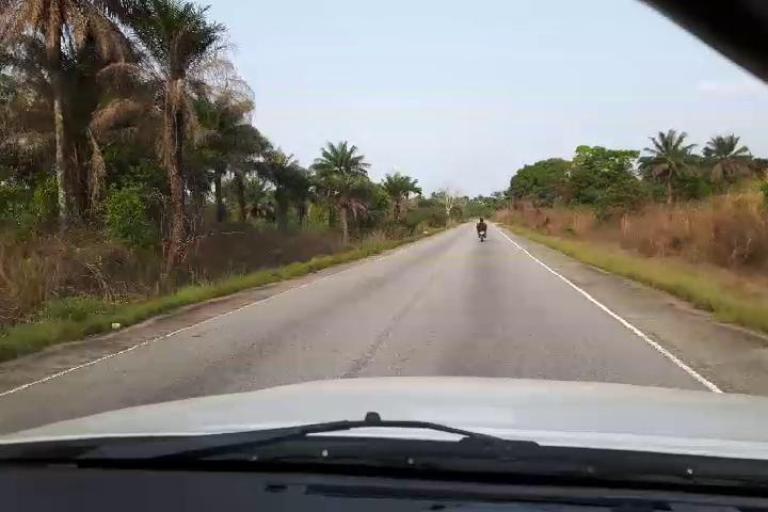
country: SL
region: Eastern Province
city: Blama
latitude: 7.9333
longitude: -11.5146
